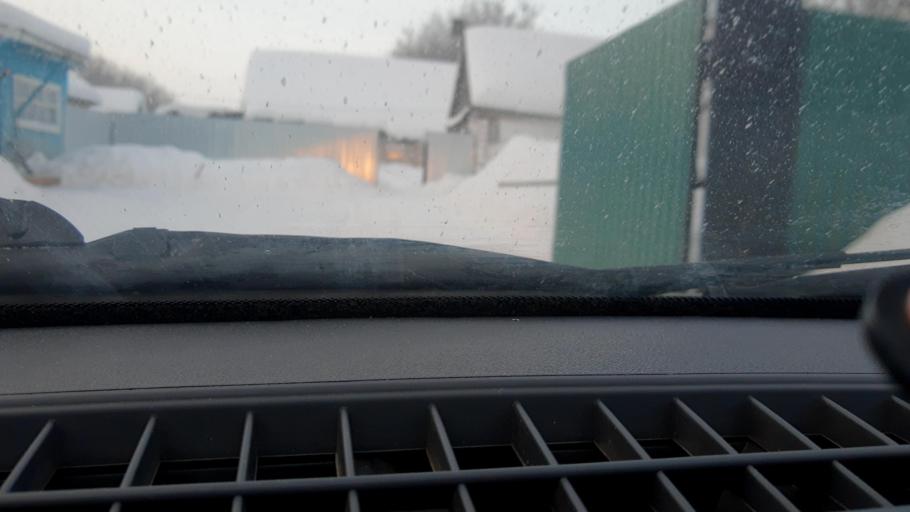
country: RU
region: Bashkortostan
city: Davlekanovo
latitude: 54.5567
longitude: 55.0124
